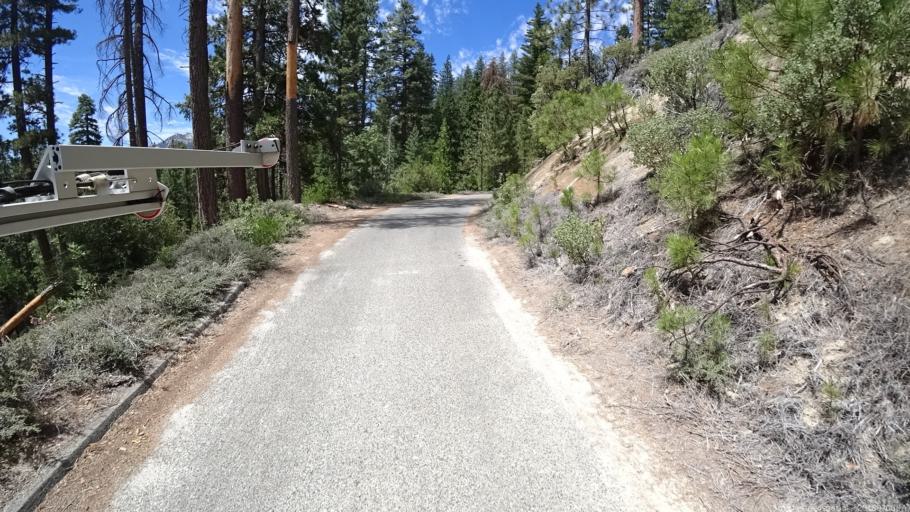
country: US
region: California
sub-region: Madera County
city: Oakhurst
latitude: 37.4122
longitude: -119.4037
